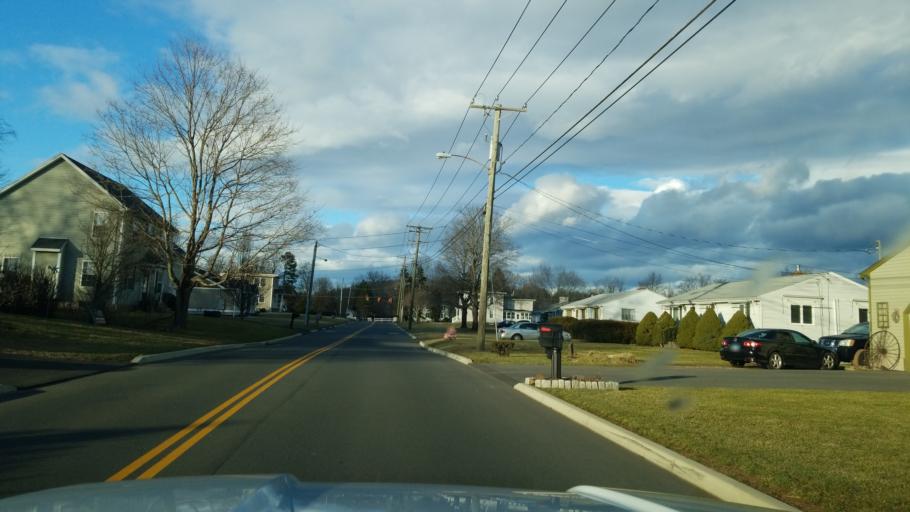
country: US
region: Connecticut
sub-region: Middlesex County
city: Middletown
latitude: 41.5319
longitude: -72.6337
